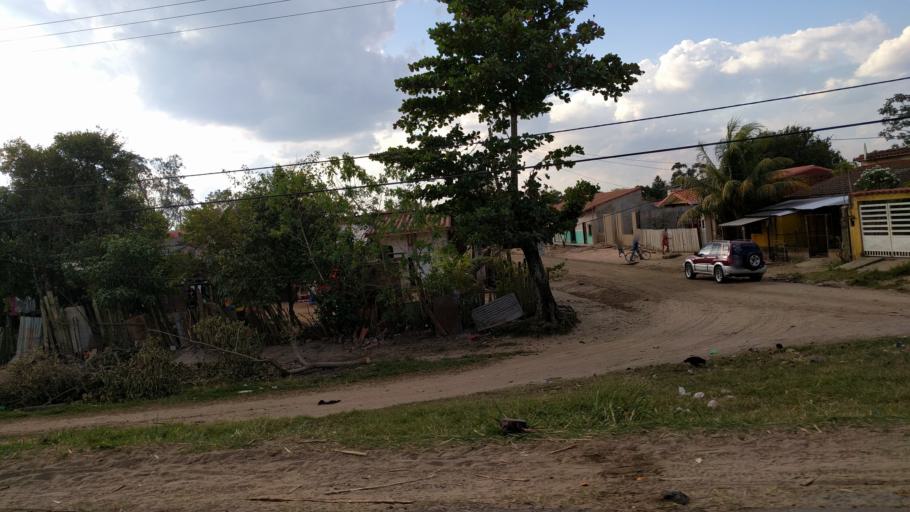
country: BO
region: Santa Cruz
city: Montero
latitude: -17.3185
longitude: -63.2721
